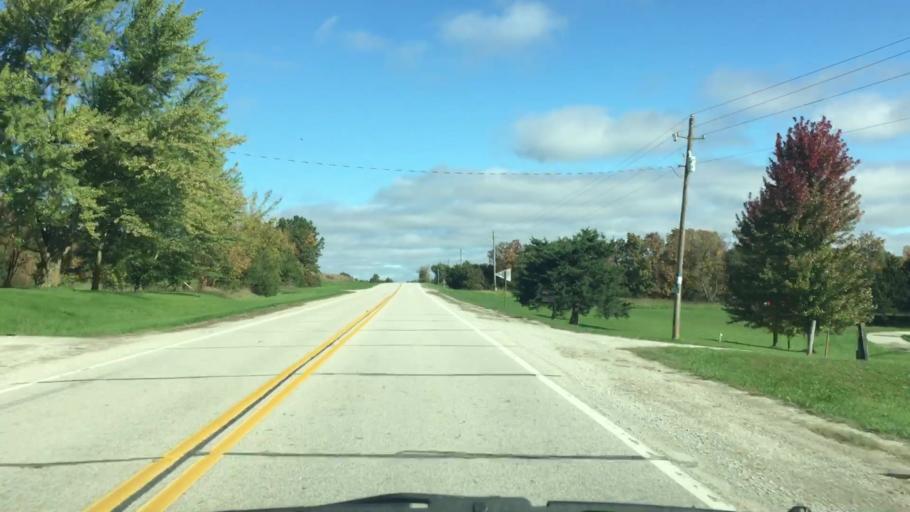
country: US
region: Iowa
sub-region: Decatur County
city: Leon
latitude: 40.6910
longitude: -93.7750
